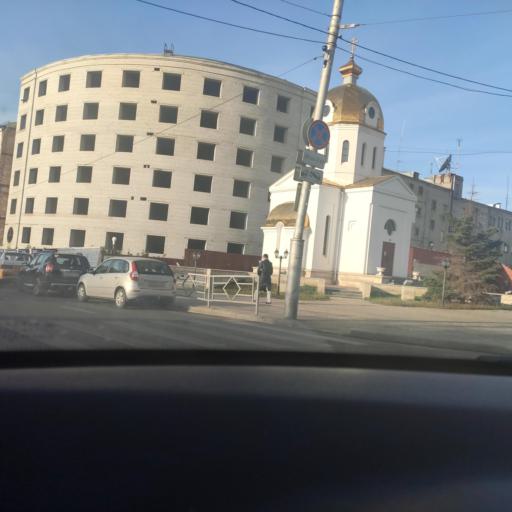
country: RU
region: Samara
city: Rozhdestveno
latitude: 53.1831
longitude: 50.0861
